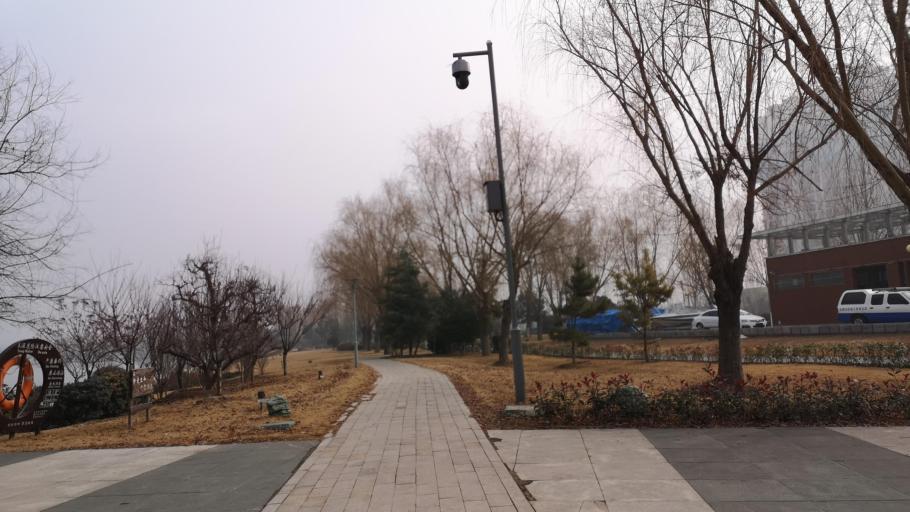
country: CN
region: Henan Sheng
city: Zhongyuanlu
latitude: 35.8004
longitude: 115.0523
